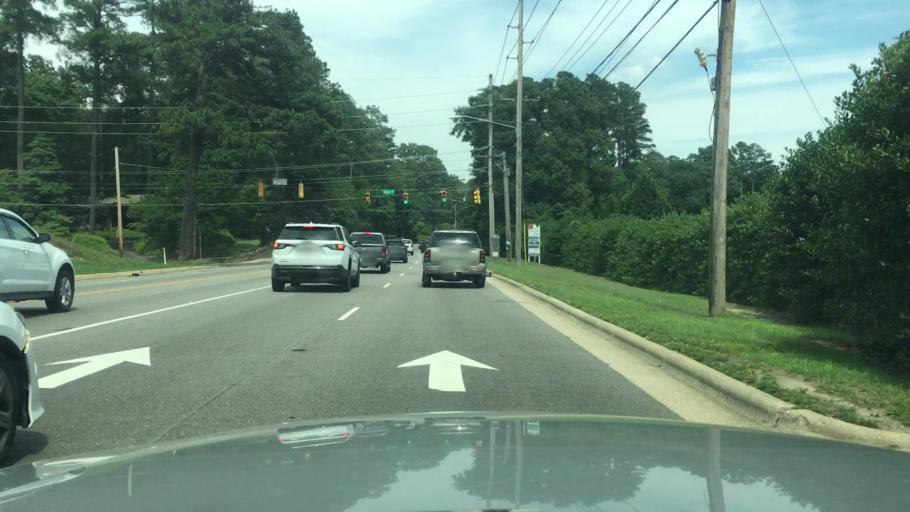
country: US
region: North Carolina
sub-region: Cumberland County
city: Fayetteville
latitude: 35.0639
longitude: -78.9276
